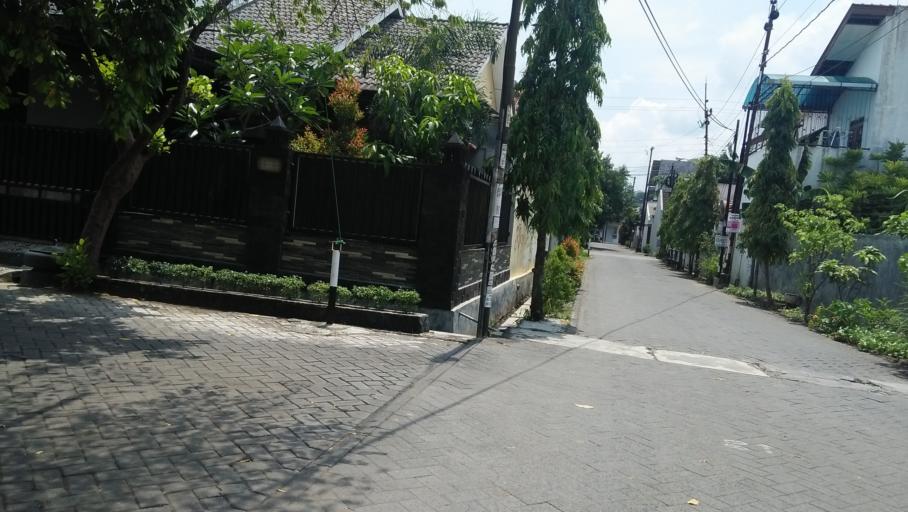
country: ID
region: Central Java
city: Mranggen
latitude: -7.0294
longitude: 110.4622
